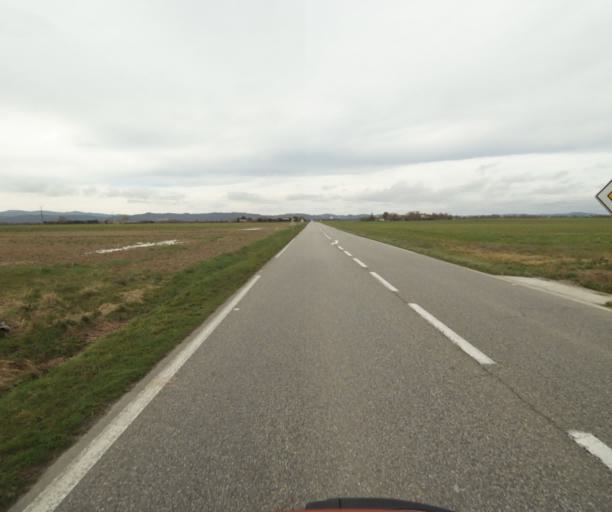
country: FR
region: Midi-Pyrenees
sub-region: Departement de l'Ariege
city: La Tour-du-Crieu
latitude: 43.0925
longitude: 1.6791
